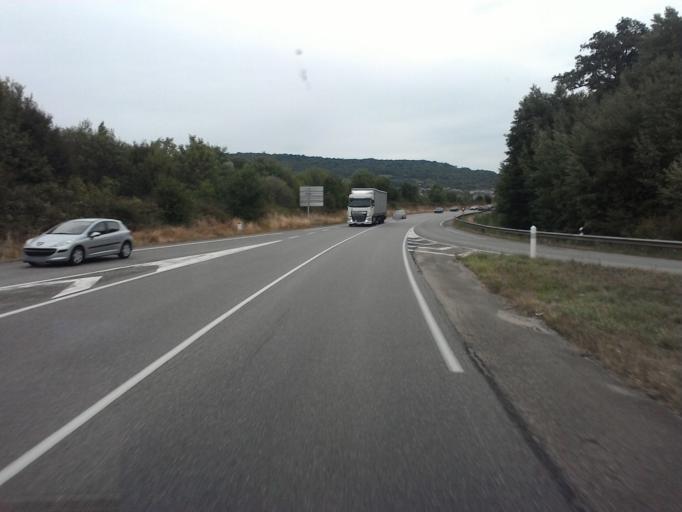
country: FR
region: Lorraine
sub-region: Departement de Meurthe-et-Moselle
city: Pont-Saint-Vincent
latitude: 48.6006
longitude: 6.1165
